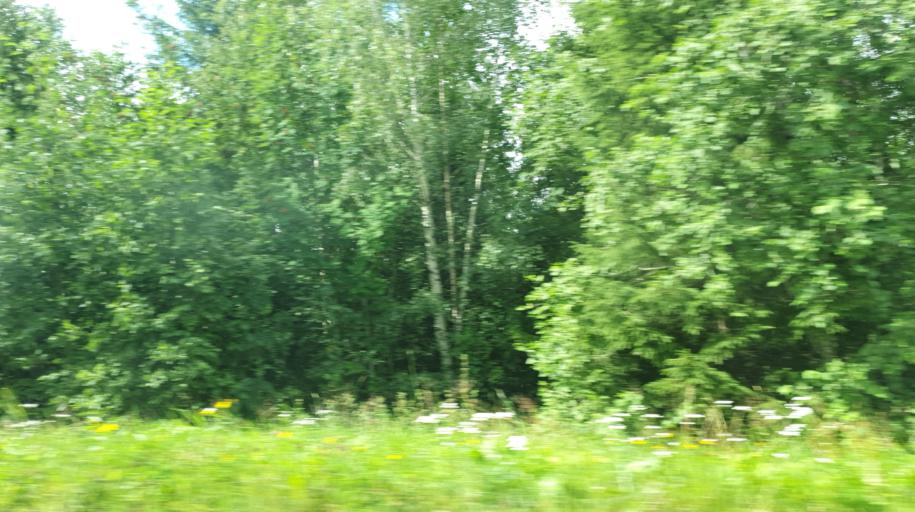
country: NO
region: Nord-Trondelag
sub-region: Levanger
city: Skogn
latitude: 63.6101
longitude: 11.2763
